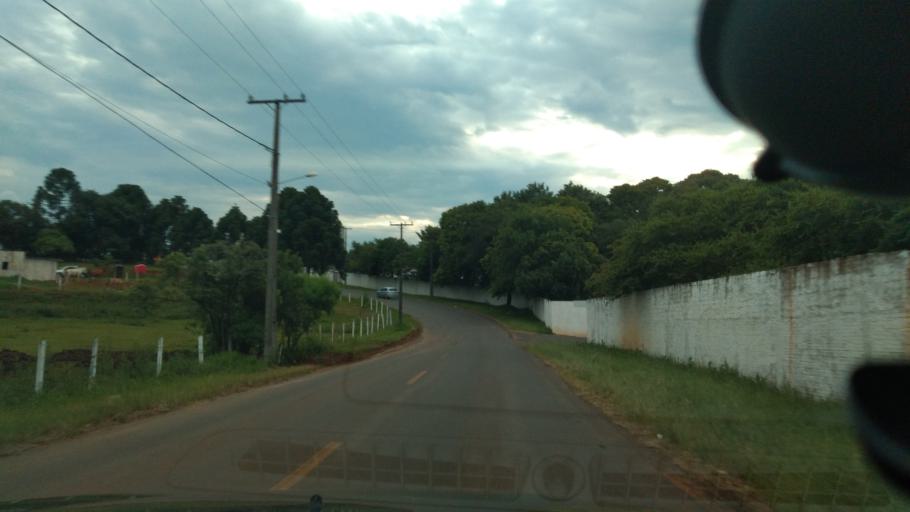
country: BR
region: Parana
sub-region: Guarapuava
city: Guarapuava
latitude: -25.3899
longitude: -51.4849
